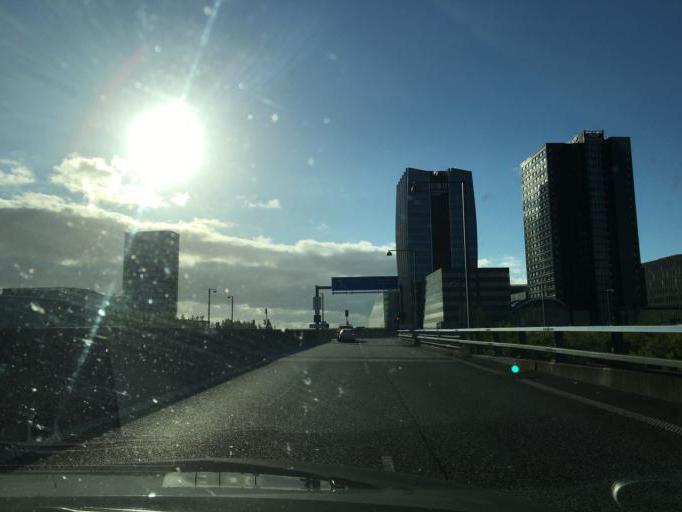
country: DK
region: Capital Region
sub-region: Tarnby Kommune
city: Tarnby
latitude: 55.6281
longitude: 12.5732
